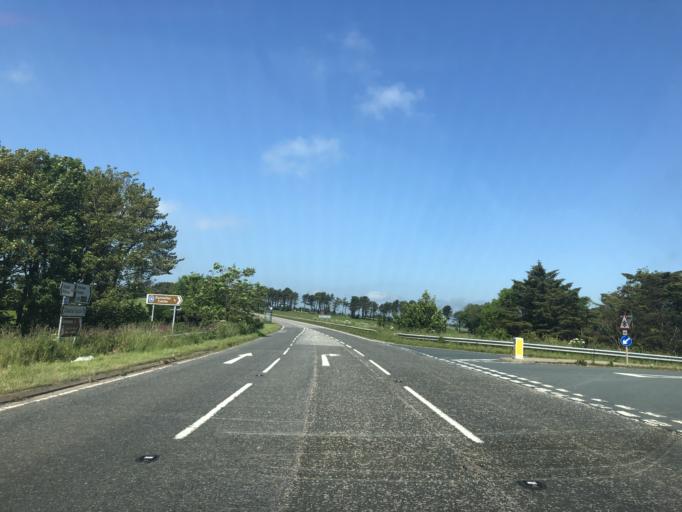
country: GB
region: Scotland
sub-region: Aberdeenshire
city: Stonehaven
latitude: 56.9418
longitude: -2.2077
